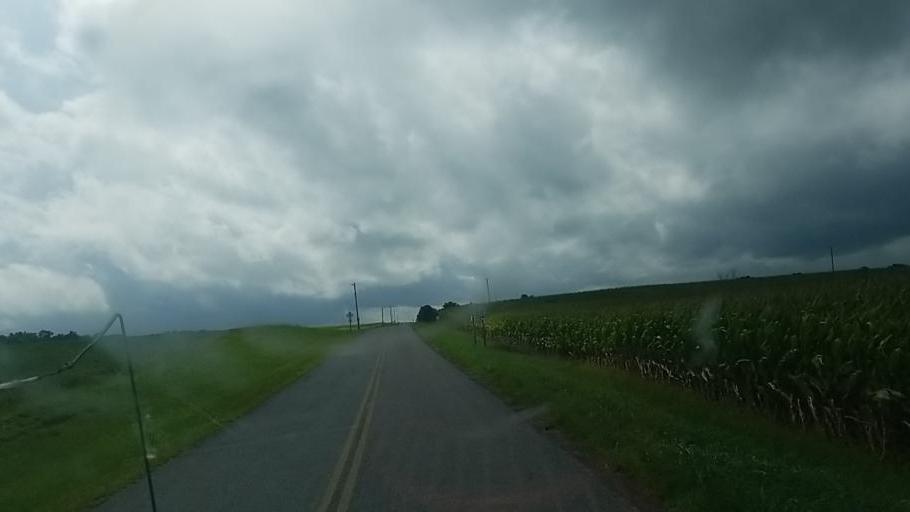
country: US
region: Ohio
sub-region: Champaign County
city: North Lewisburg
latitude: 40.2526
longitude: -83.6522
